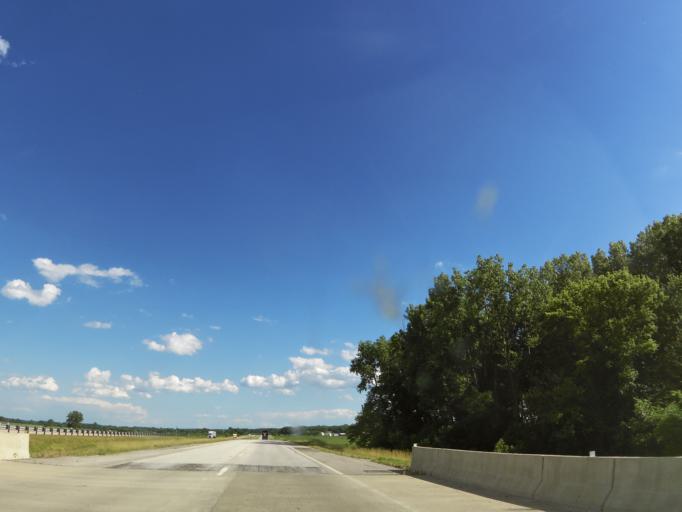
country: US
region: Illinois
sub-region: Hancock County
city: Warsaw
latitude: 40.2990
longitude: -91.5719
